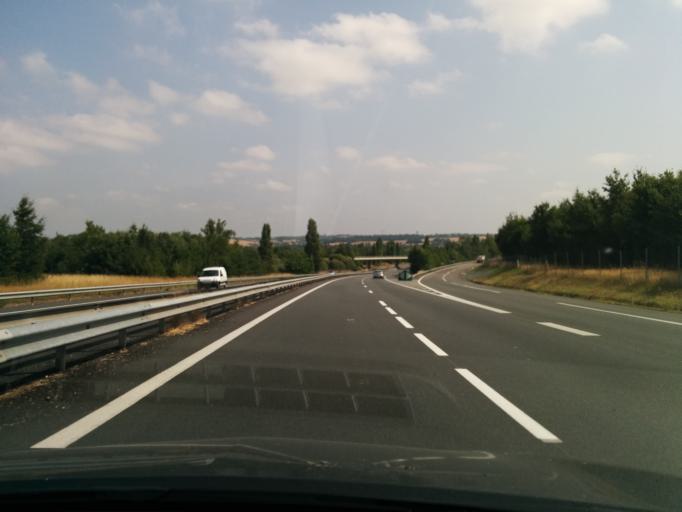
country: FR
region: Midi-Pyrenees
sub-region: Departement de la Haute-Garonne
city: Gragnague
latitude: 43.6839
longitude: 1.5622
